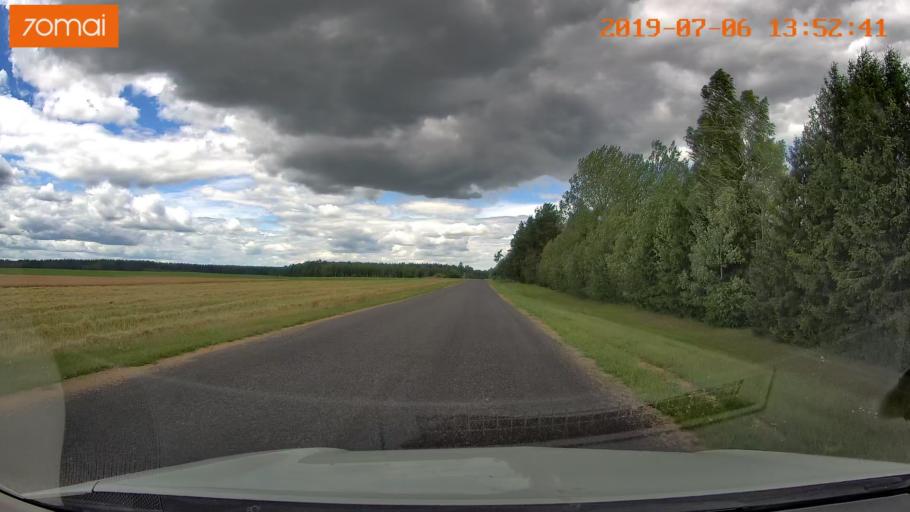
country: BY
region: Minsk
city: Ivyanyets
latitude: 53.7241
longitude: 26.8280
